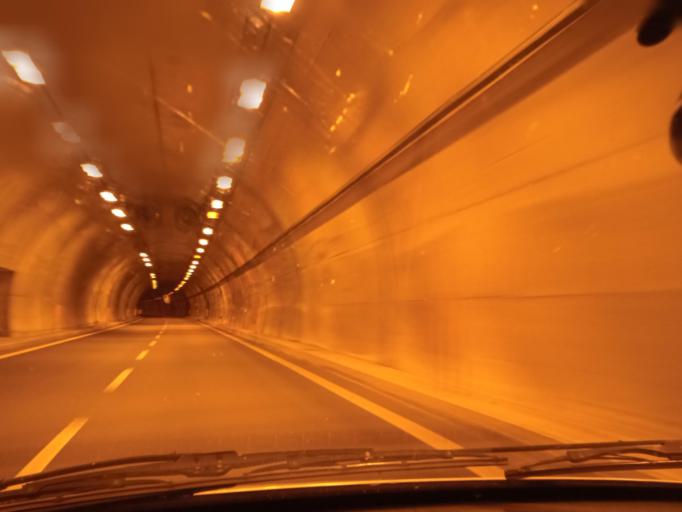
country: IT
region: Sicily
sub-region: Messina
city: Caronia
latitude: 38.0192
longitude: 14.4397
